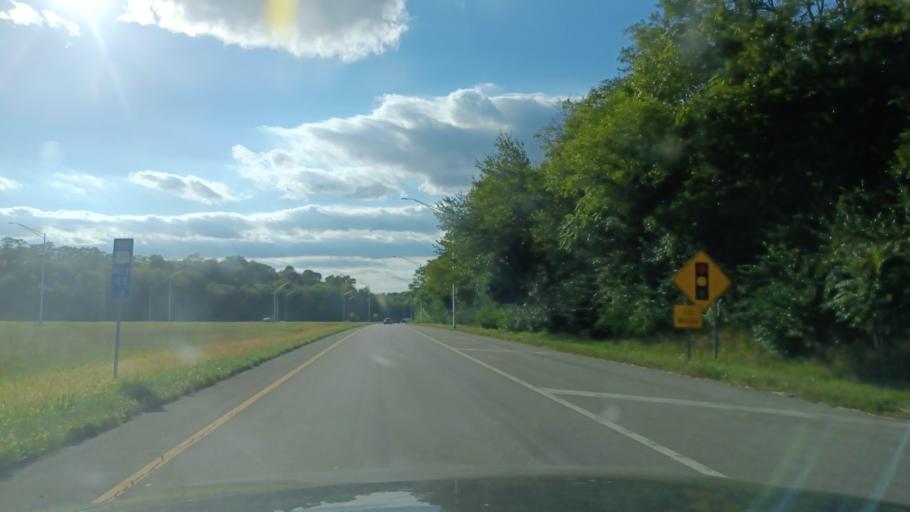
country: US
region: Ohio
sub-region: Greene County
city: Xenia
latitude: 39.6941
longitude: -83.9766
